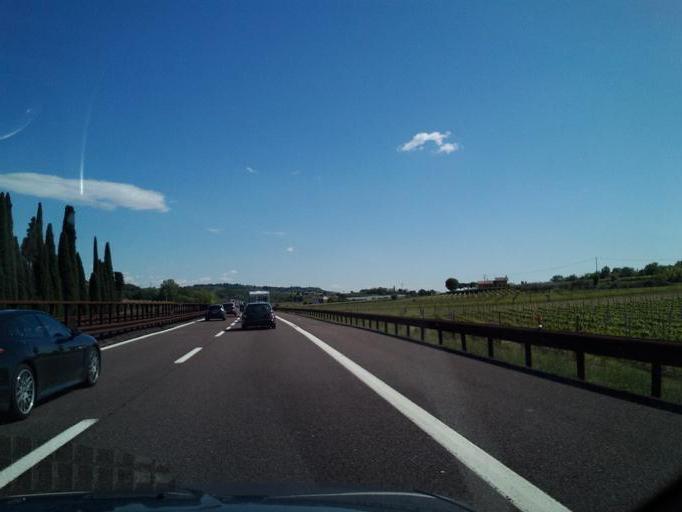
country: IT
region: Veneto
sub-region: Provincia di Verona
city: Pastrengo
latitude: 45.4985
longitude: 10.7857
